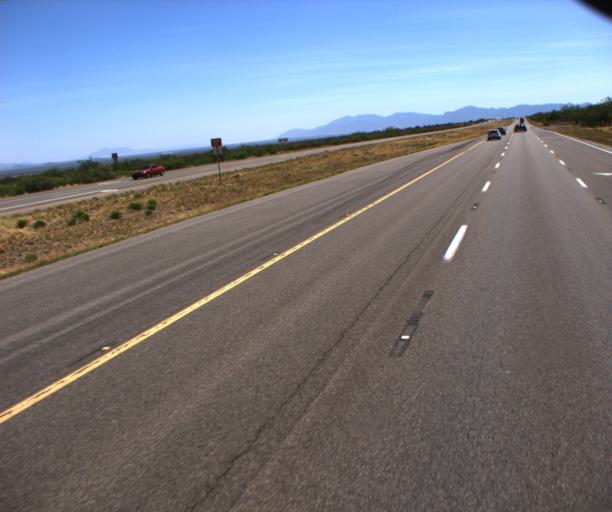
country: US
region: Arizona
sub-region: Cochise County
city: Whetstone
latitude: 31.8346
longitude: -110.3439
